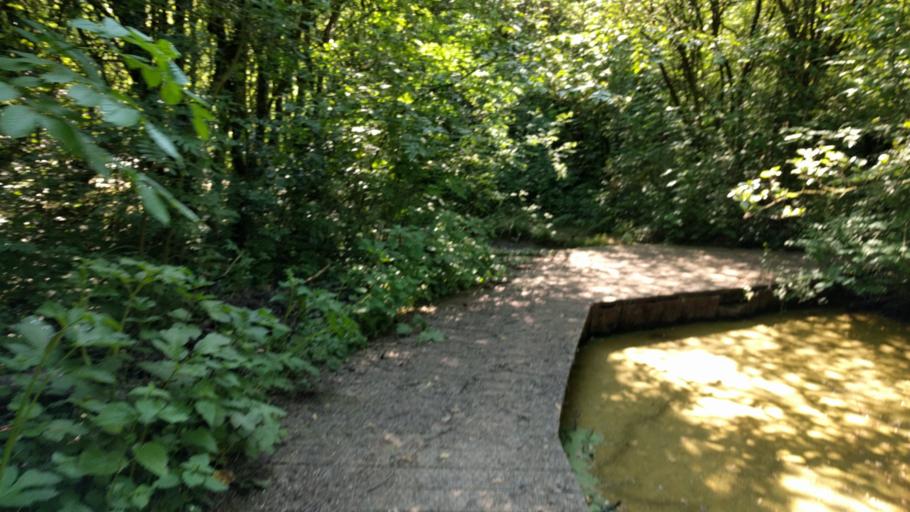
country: GB
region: England
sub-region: Warrington
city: Croft
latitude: 53.4188
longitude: -2.5314
